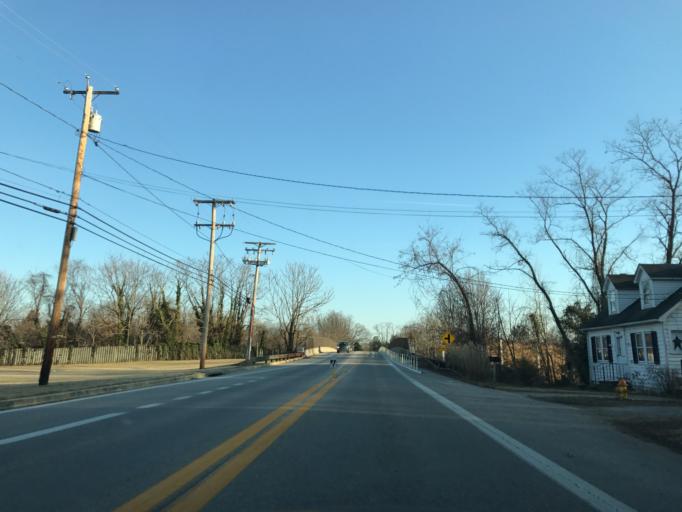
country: US
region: Maryland
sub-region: Anne Arundel County
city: Parole
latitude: 38.9965
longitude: -76.5141
